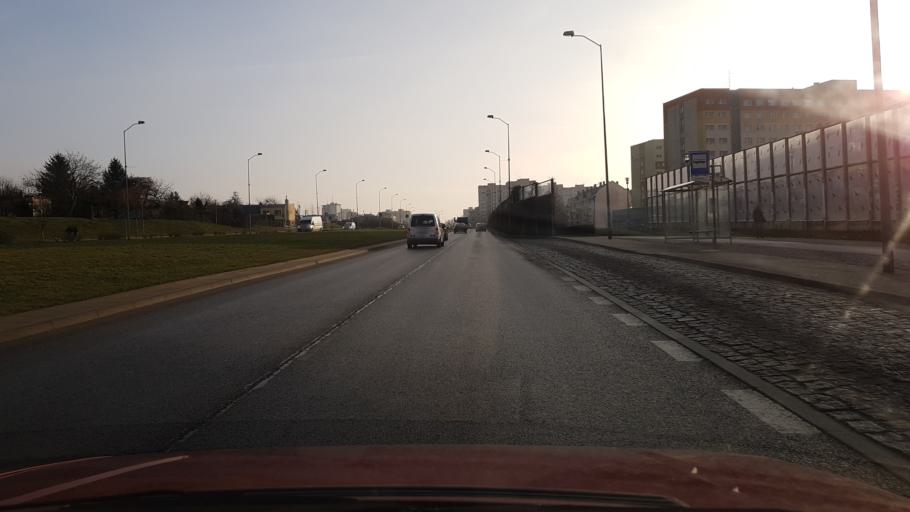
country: PL
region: West Pomeranian Voivodeship
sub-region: Szczecin
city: Szczecin
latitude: 53.4547
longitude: 14.5448
